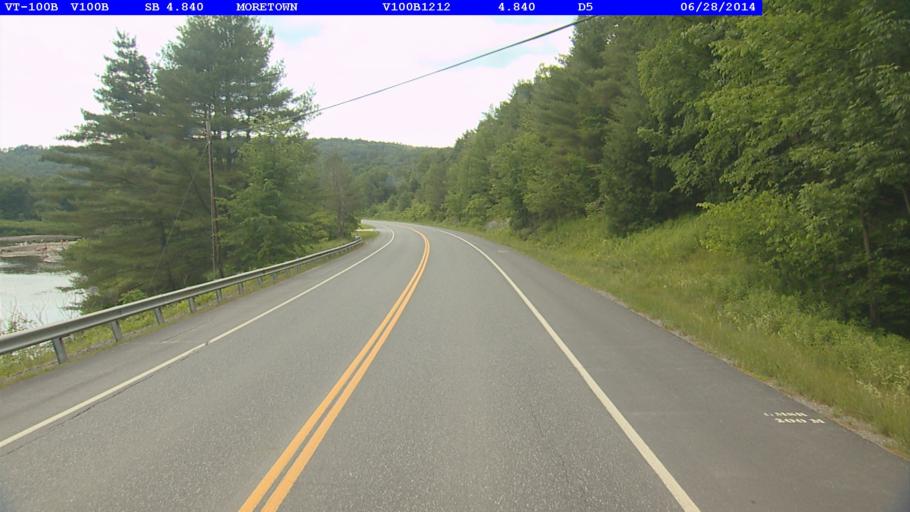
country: US
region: Vermont
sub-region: Washington County
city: Waterbury
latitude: 44.2908
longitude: -72.7221
